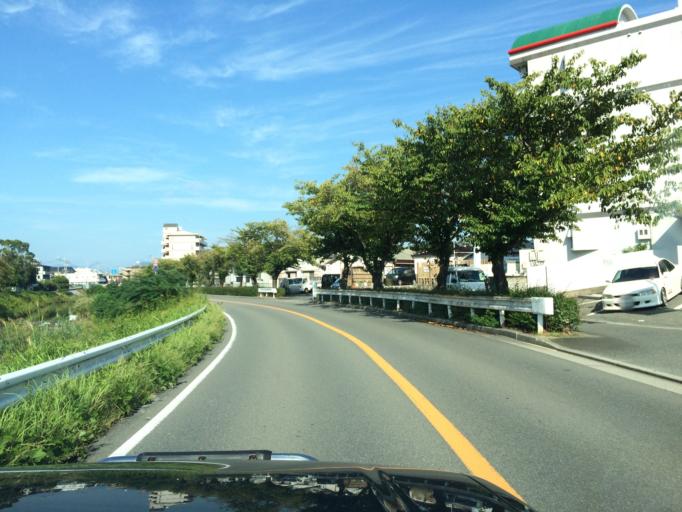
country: JP
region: Hyogo
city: Itami
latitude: 34.7876
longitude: 135.3883
